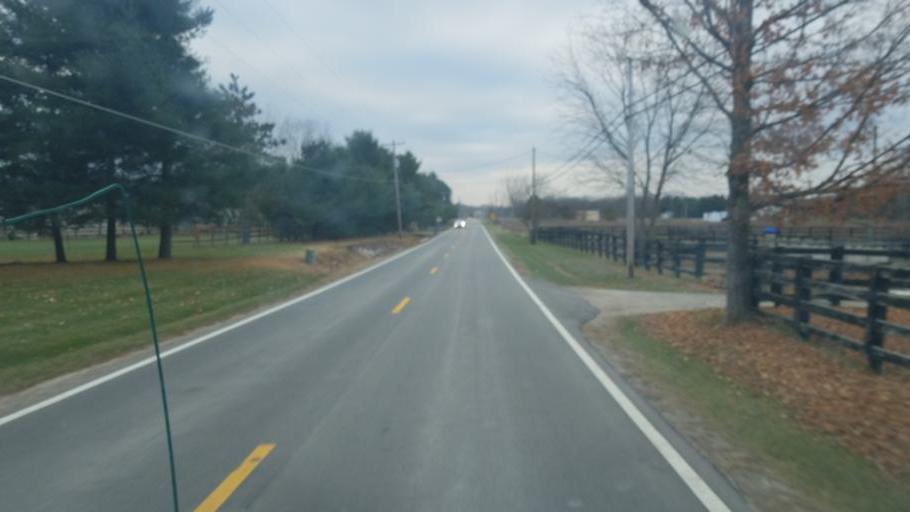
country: US
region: Ohio
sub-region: Delaware County
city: Ashley
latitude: 40.3306
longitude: -82.9405
